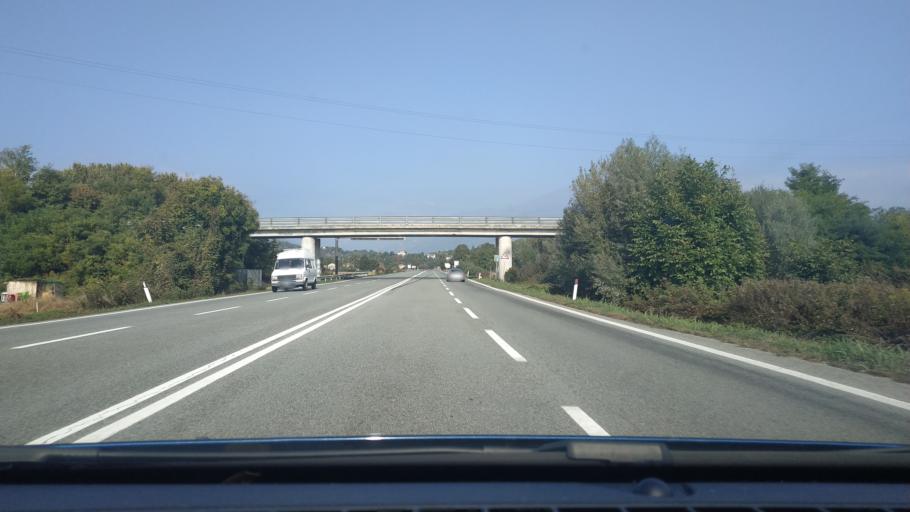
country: IT
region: Piedmont
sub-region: Provincia di Torino
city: Pavone Canavese
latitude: 45.4341
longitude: 7.8854
